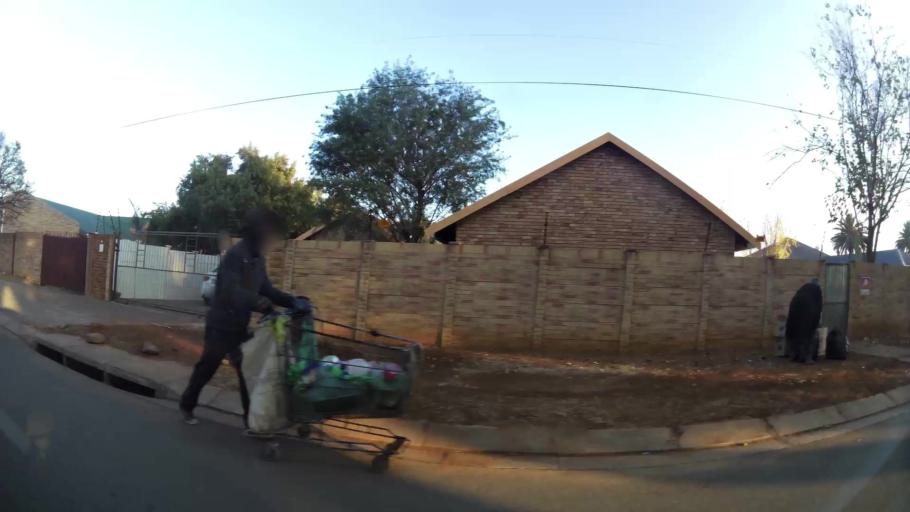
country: ZA
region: Orange Free State
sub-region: Mangaung Metropolitan Municipality
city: Bloemfontein
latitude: -29.0861
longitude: 26.1615
